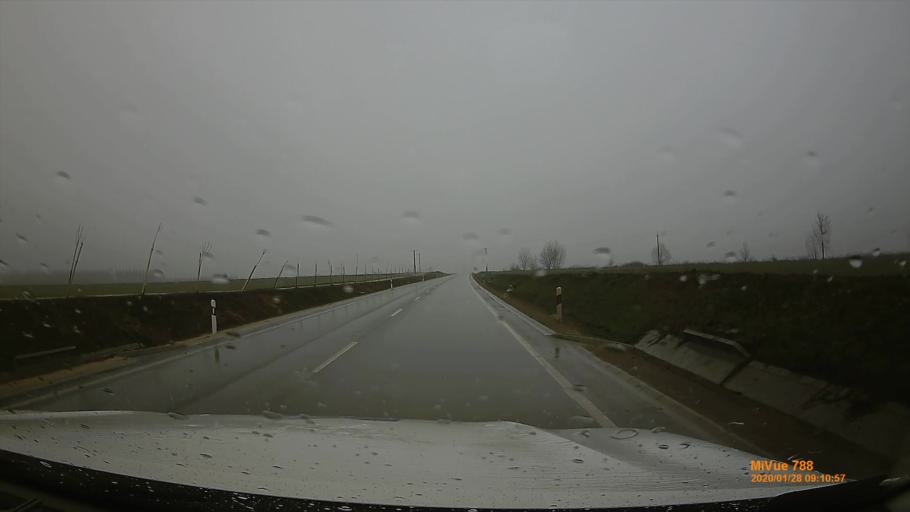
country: HU
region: Pest
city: Pilis
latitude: 47.3084
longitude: 19.5459
